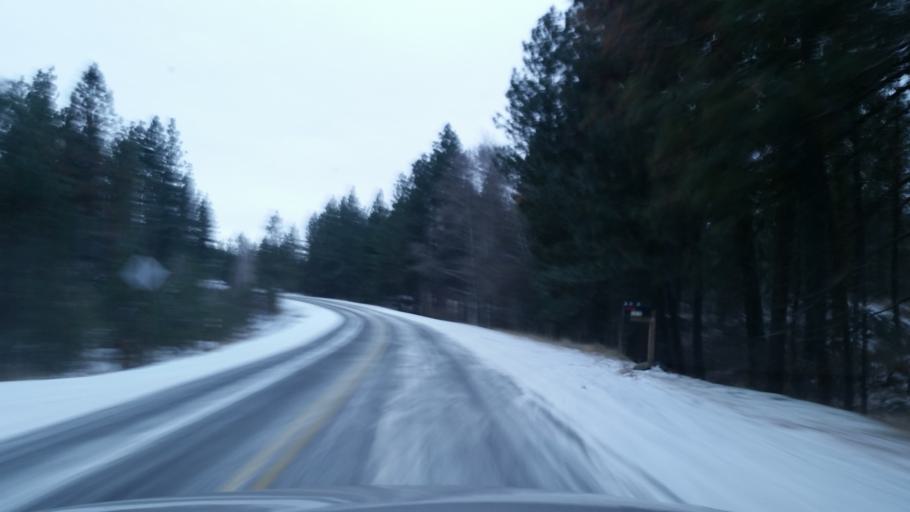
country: US
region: Washington
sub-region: Spokane County
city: Cheney
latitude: 47.4487
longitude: -117.5236
